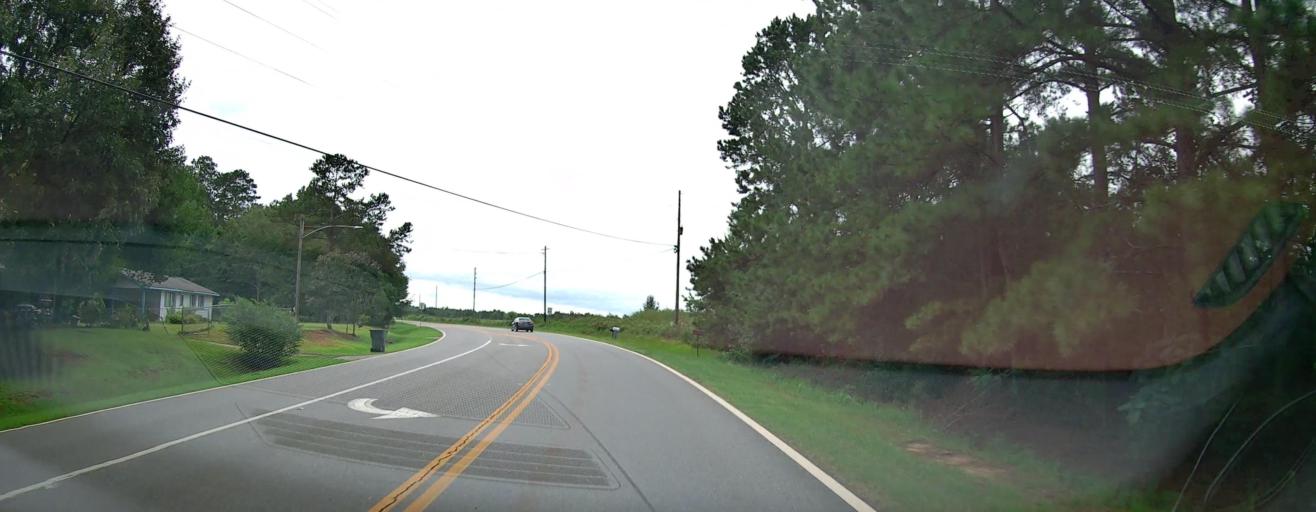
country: US
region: Georgia
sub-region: Twiggs County
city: Jeffersonville
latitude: 32.6807
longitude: -83.3537
